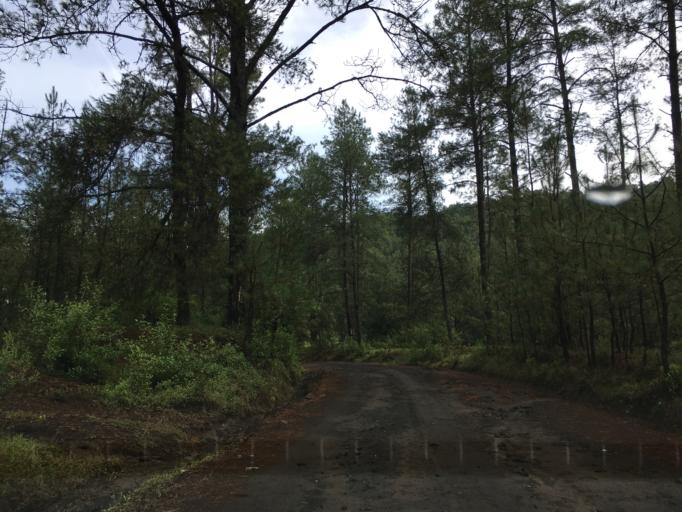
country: MX
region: Michoacan
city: Angahuan
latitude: 19.5056
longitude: -102.2119
